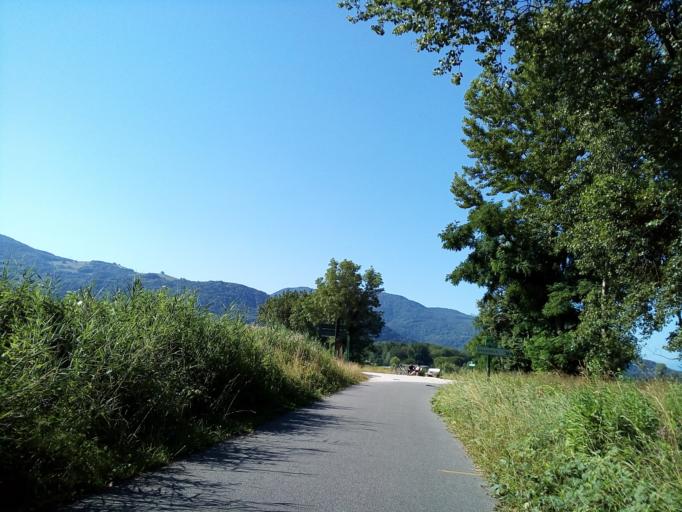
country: FR
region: Rhone-Alpes
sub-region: Departement de l'Isere
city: Meylan
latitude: 45.2040
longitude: 5.7957
